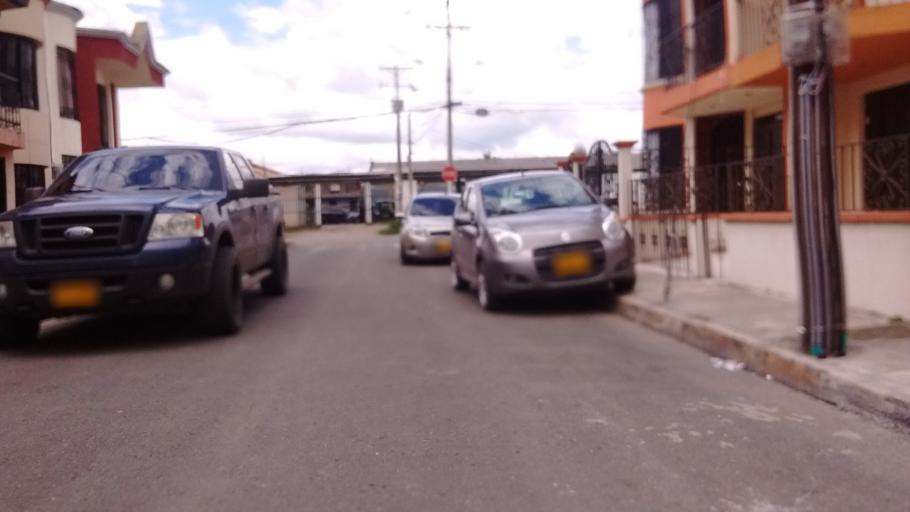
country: CO
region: Cauca
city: Popayan
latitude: 2.4605
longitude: -76.5912
